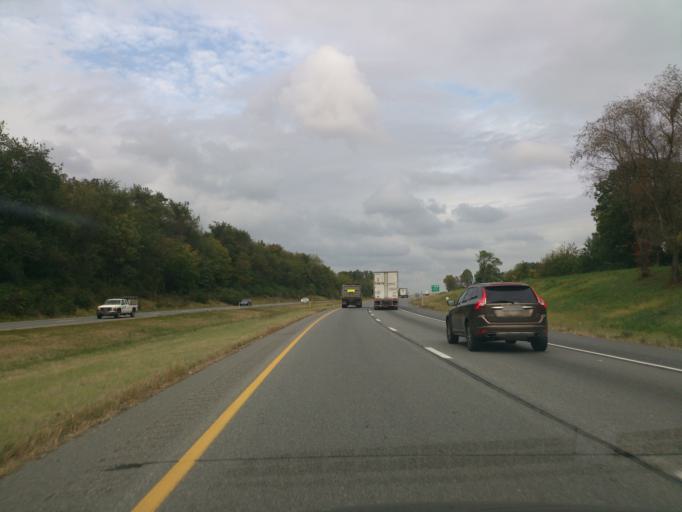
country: US
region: Pennsylvania
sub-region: Lancaster County
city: Reamstown
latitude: 40.2060
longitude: -76.1159
